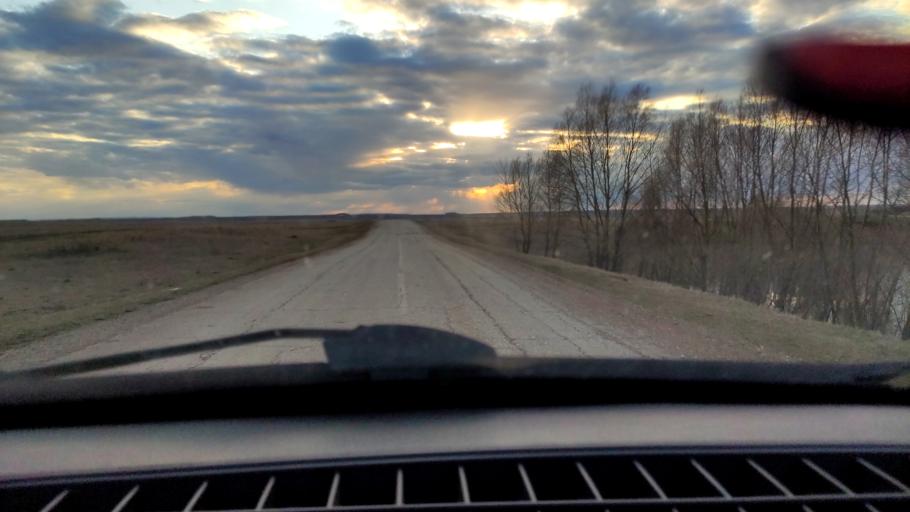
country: RU
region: Bashkortostan
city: Tolbazy
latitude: 54.0139
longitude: 55.5553
